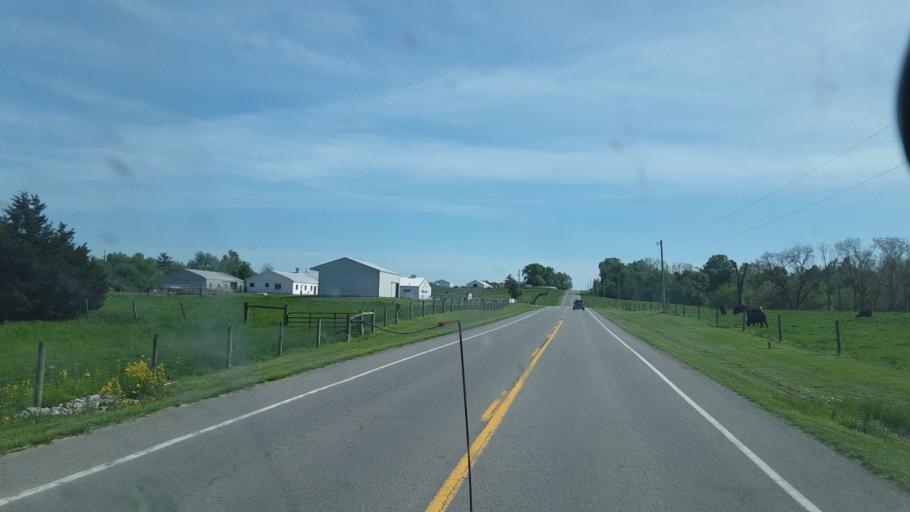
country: US
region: Illinois
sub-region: Jackson County
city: Carbondale
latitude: 37.6979
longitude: -89.2472
